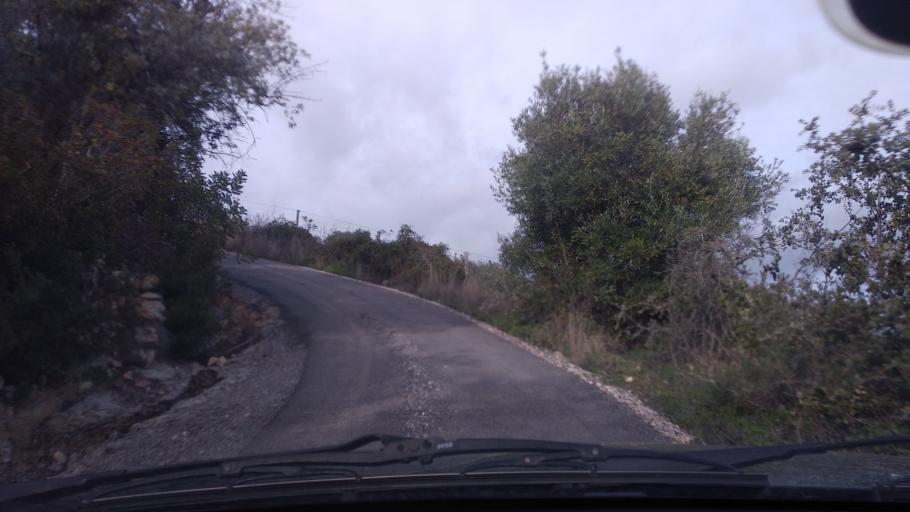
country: PT
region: Faro
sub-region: Sao Bras de Alportel
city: Sao Bras de Alportel
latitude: 37.1159
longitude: -7.9095
